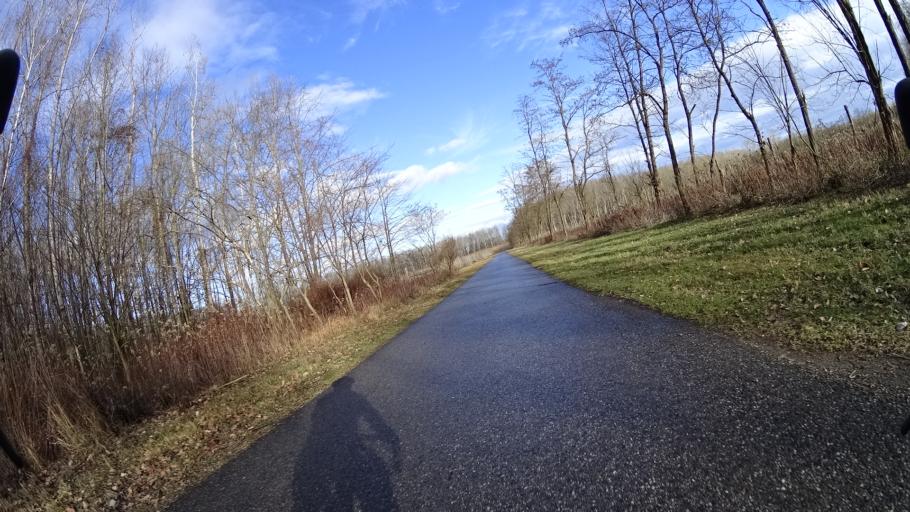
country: AT
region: Lower Austria
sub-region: Politischer Bezirk Tulln
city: Fels am Wagram
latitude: 48.3716
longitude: 15.8463
